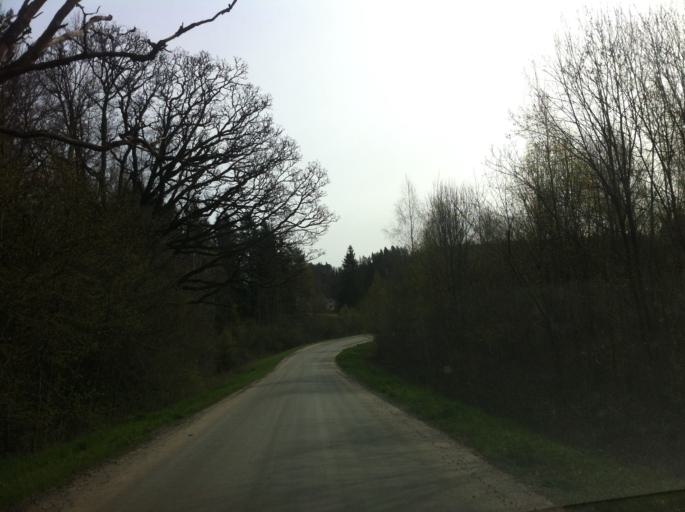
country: SE
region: Vaestra Goetaland
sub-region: Bollebygds Kommun
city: Bollebygd
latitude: 57.7511
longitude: 12.6004
